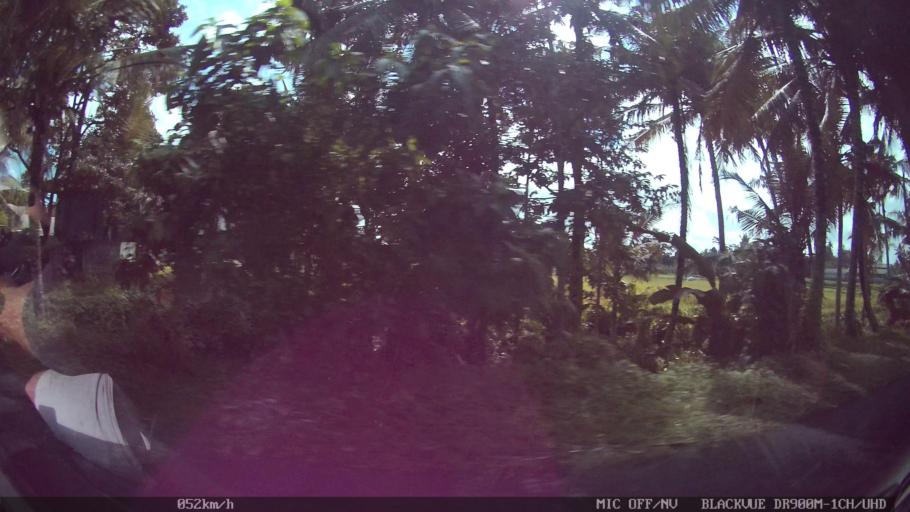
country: ID
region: Bali
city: Banjar Kelodan
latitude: -8.5215
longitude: 115.3298
